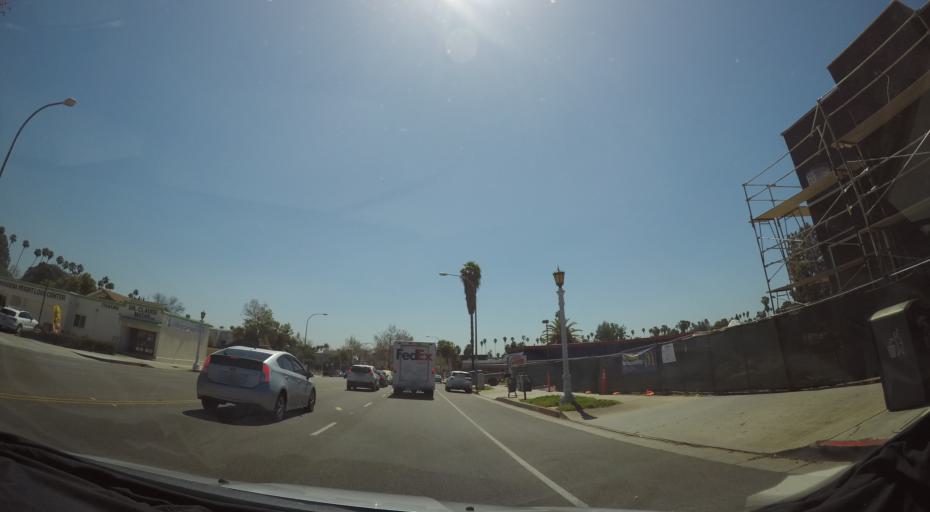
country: US
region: California
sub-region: Los Angeles County
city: Pasadena
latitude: 34.1597
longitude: -118.1326
